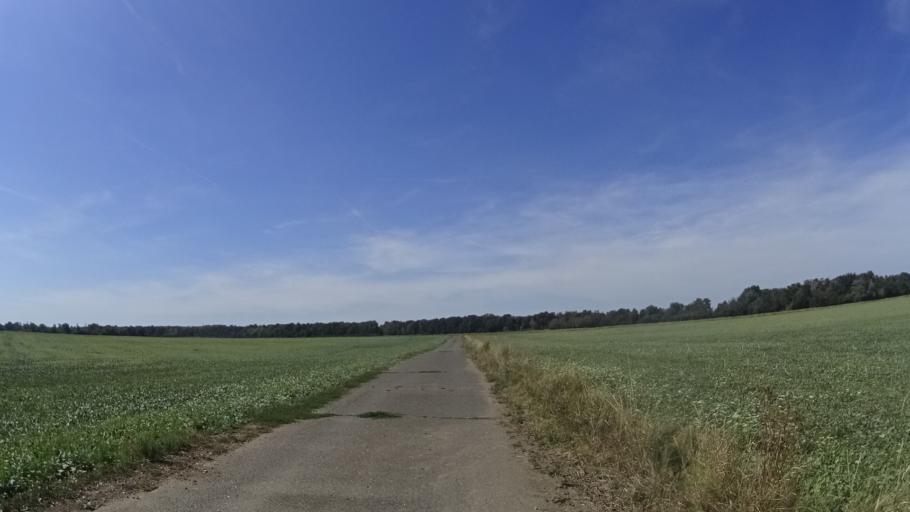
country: AT
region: Lower Austria
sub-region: Politischer Bezirk Ganserndorf
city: Angern an der March
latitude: 48.3654
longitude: 16.8674
